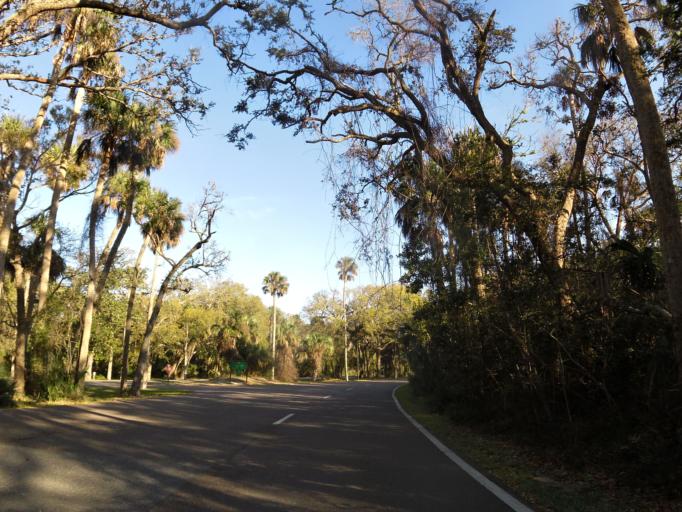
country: US
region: Florida
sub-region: Duval County
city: Atlantic Beach
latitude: 30.3718
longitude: -81.4015
